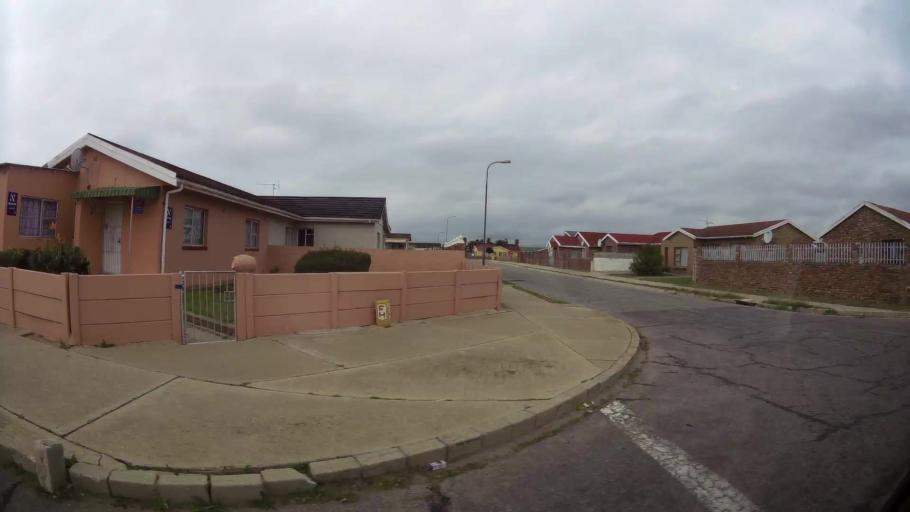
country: ZA
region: Eastern Cape
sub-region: Nelson Mandela Bay Metropolitan Municipality
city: Port Elizabeth
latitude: -33.8996
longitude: 25.5612
